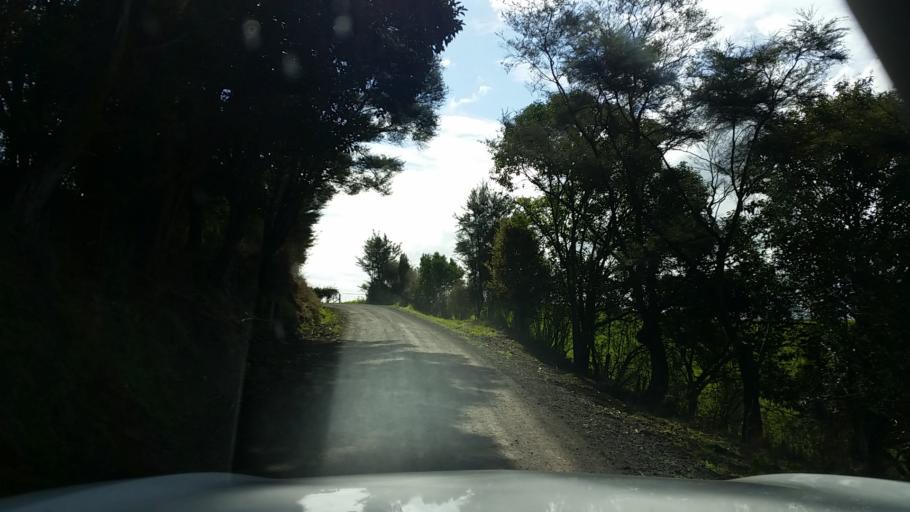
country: NZ
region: Waikato
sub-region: Hauraki District
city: Ngatea
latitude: -37.4405
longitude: 175.4821
